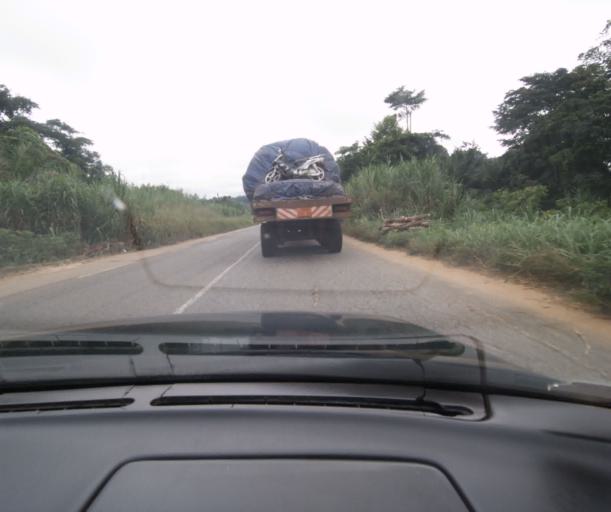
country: CM
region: Centre
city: Ombesa
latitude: 4.5745
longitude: 11.2666
